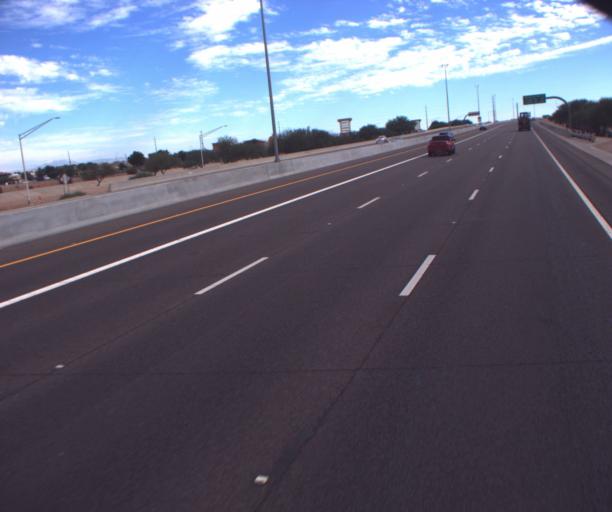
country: US
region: Arizona
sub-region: Maricopa County
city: Chandler
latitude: 33.2871
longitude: -111.8446
